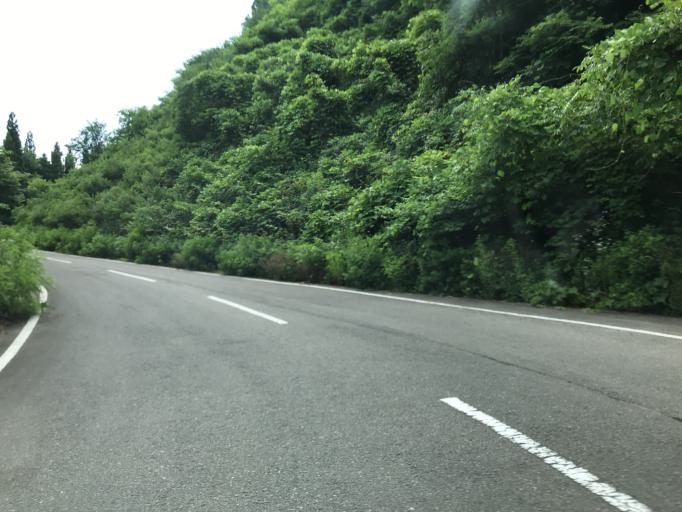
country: JP
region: Fukushima
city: Yanagawamachi-saiwaicho
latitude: 37.7614
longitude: 140.6828
